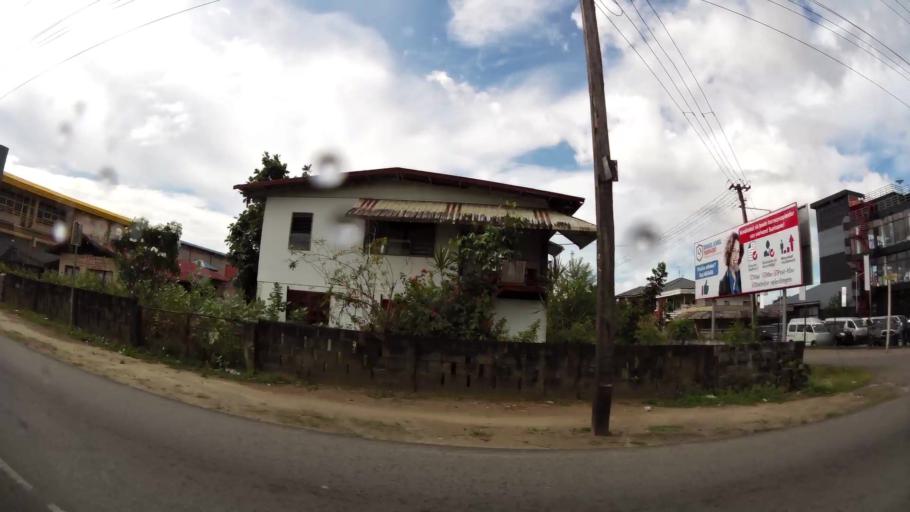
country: SR
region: Paramaribo
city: Paramaribo
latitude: 5.8419
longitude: -55.1937
